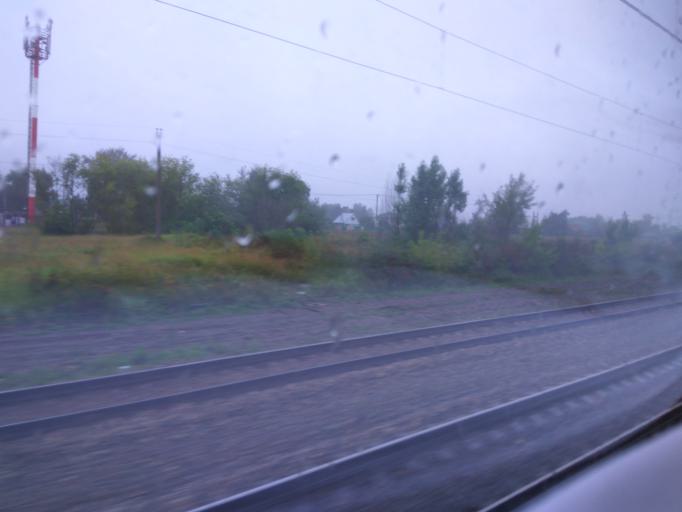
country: RU
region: Moskovskaya
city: Uzunovo
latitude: 54.6801
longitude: 38.5276
